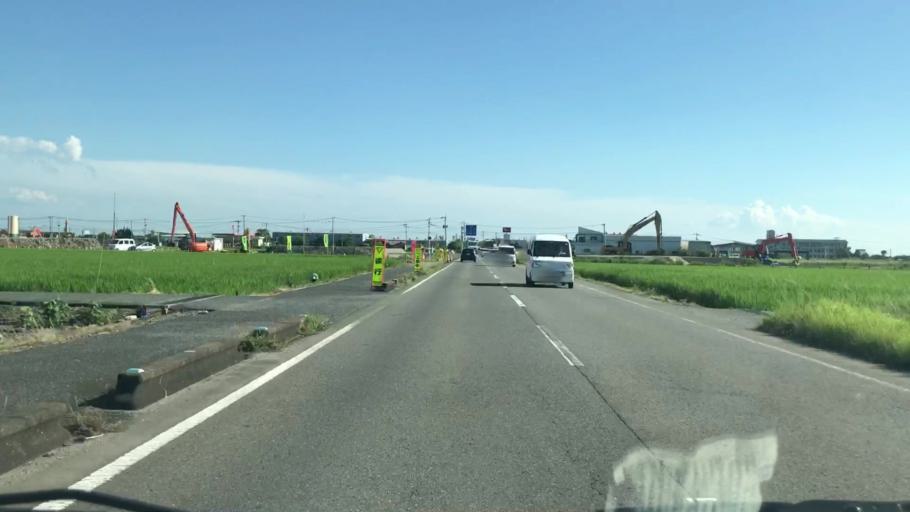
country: JP
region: Saga Prefecture
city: Okawa
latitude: 33.2159
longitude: 130.3350
